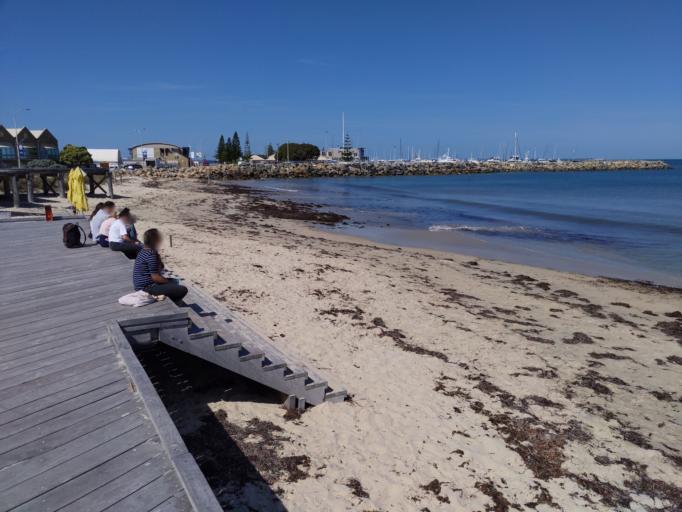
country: AU
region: Western Australia
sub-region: Fremantle
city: South Fremantle
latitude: -32.0587
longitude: 115.7427
